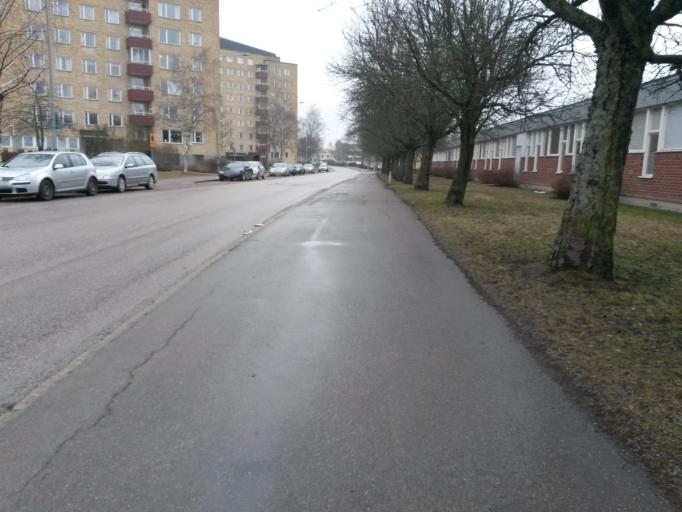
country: SE
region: Uppsala
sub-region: Uppsala Kommun
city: Uppsala
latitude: 59.8594
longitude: 17.6097
